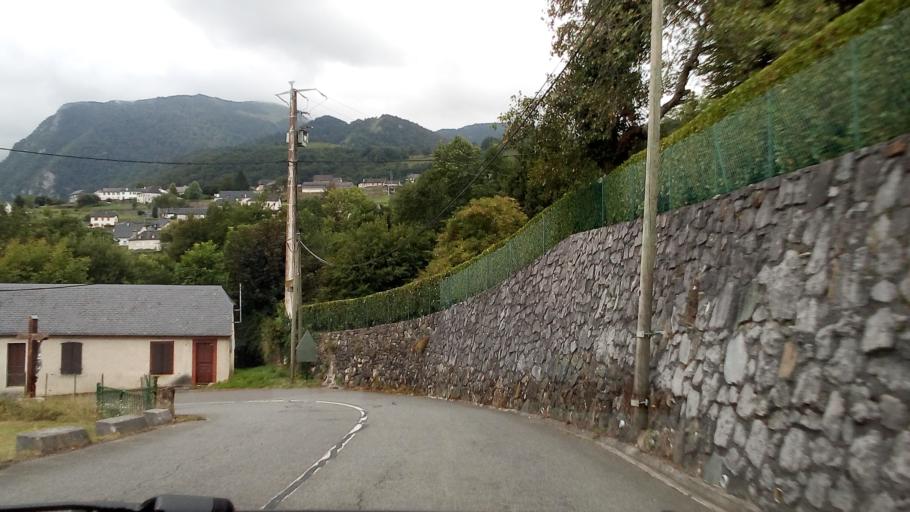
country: FR
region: Aquitaine
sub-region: Departement des Pyrenees-Atlantiques
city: Louvie-Juzon
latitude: 43.0610
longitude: -0.4448
